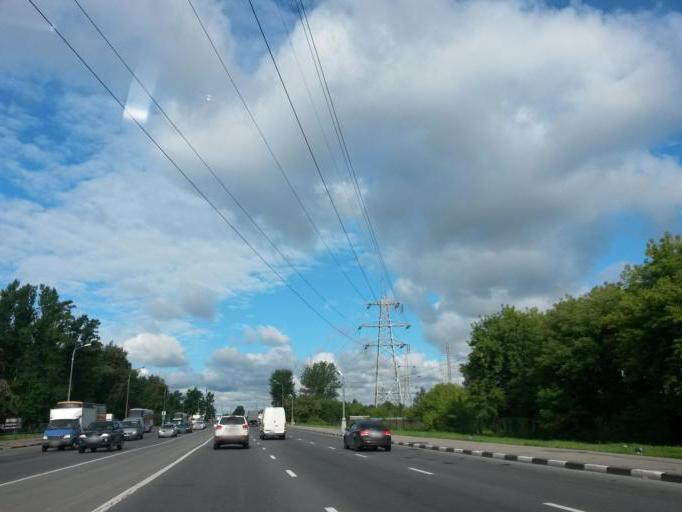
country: RU
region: Moskovskaya
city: Kotel'niki
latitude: 55.6572
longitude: 37.8223
